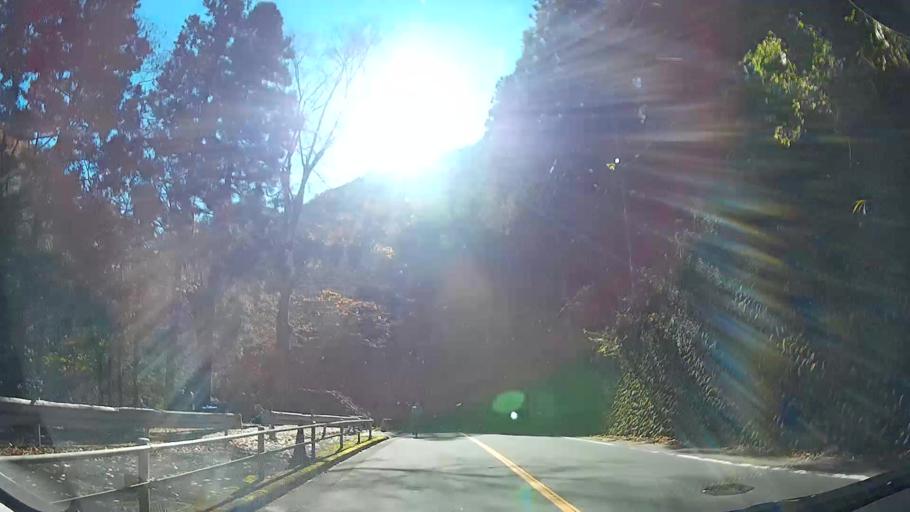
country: JP
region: Tokyo
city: Itsukaichi
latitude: 35.7111
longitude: 139.1492
